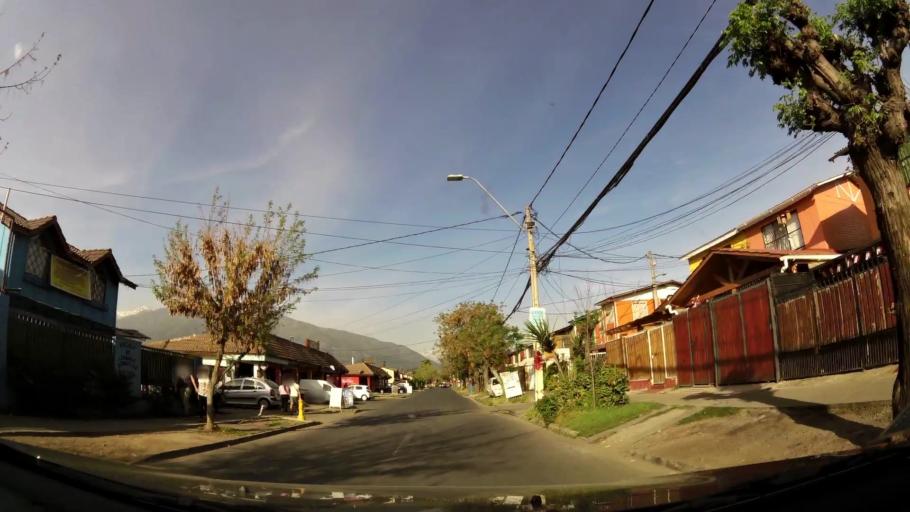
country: CL
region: Santiago Metropolitan
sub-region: Provincia de Cordillera
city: Puente Alto
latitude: -33.5886
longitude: -70.5665
